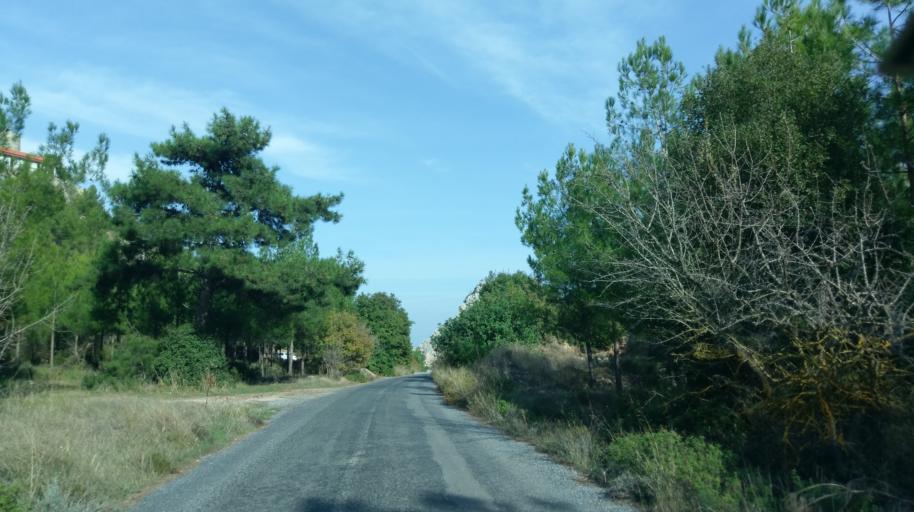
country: CY
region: Keryneia
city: Kyrenia
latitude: 35.3098
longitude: 33.2806
